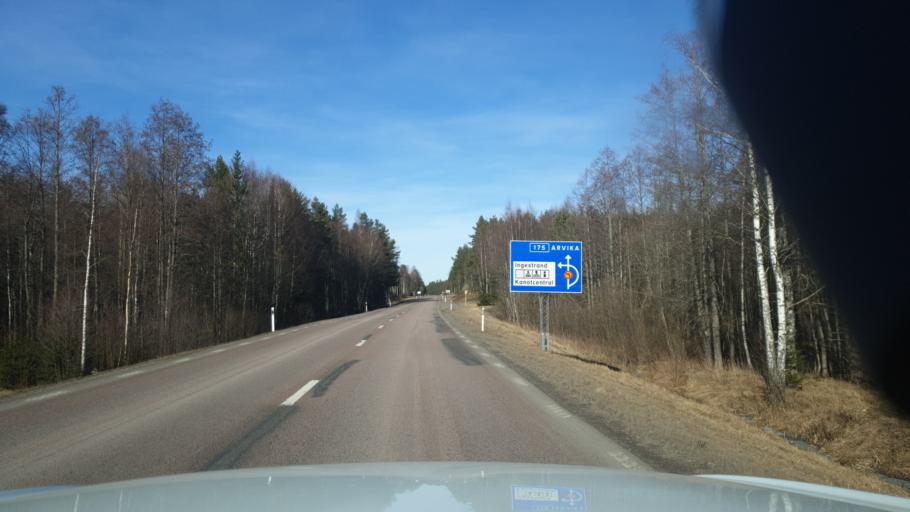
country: SE
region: Vaermland
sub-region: Arvika Kommun
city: Arvika
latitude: 59.6214
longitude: 12.6172
